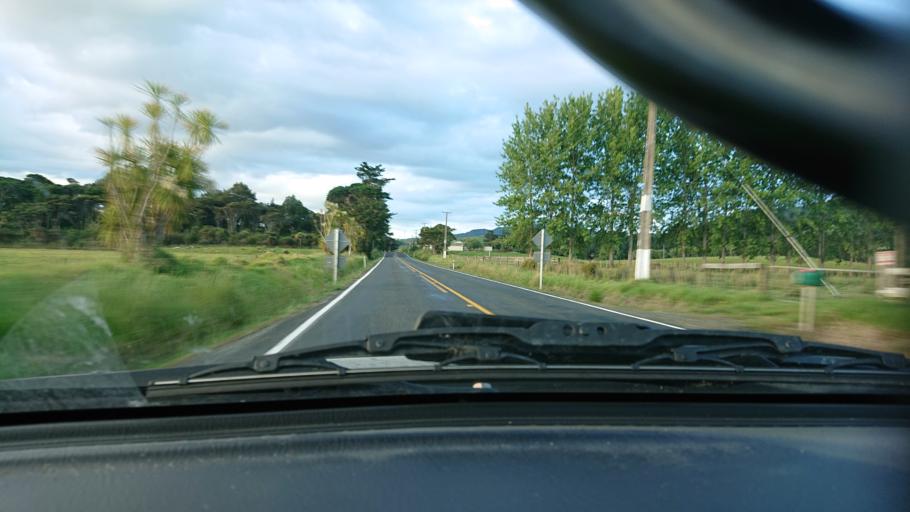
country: NZ
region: Auckland
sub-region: Auckland
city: Parakai
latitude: -36.4945
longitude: 174.4484
